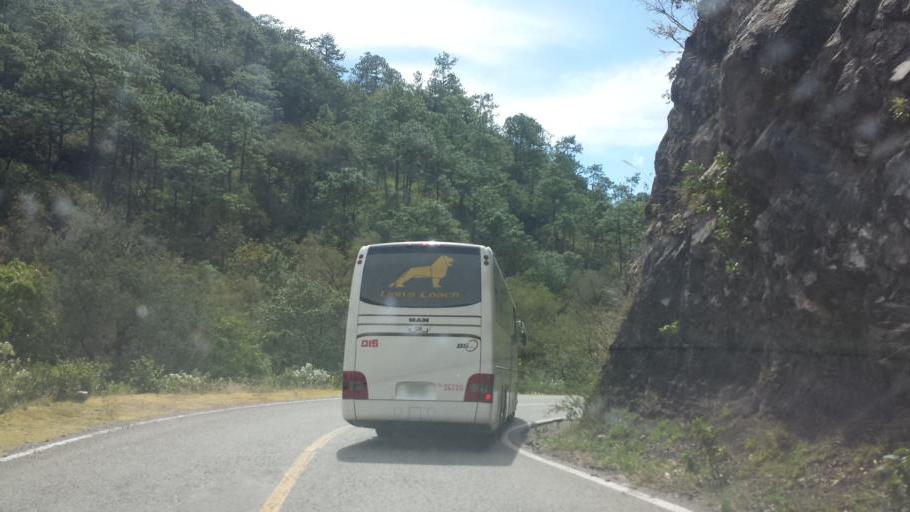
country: MX
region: Oaxaca
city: San Francisco Sola
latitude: 16.4426
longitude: -97.0328
